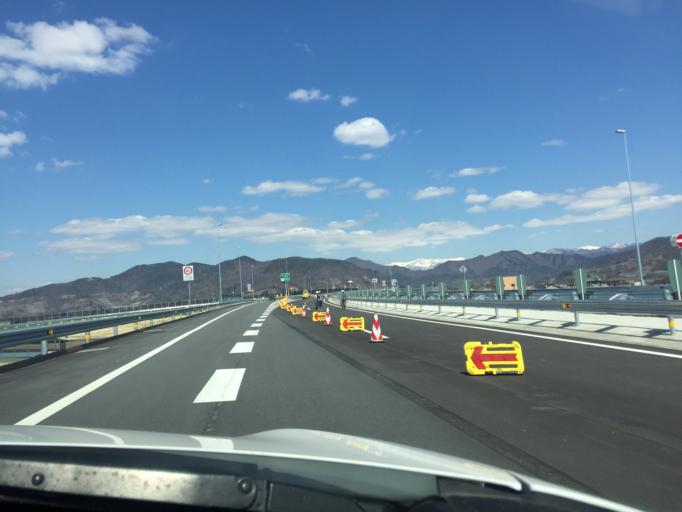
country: JP
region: Yamagata
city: Takahata
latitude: 38.0241
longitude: 140.1625
